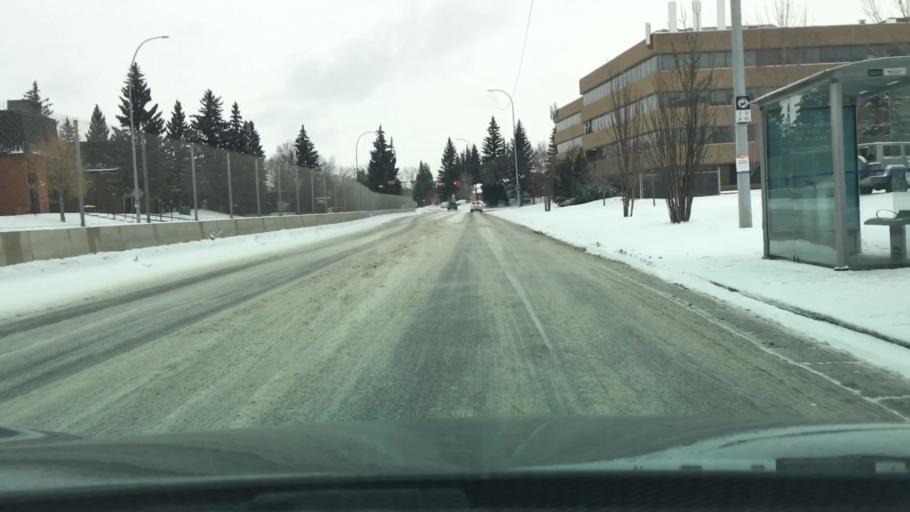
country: CA
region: Alberta
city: Calgary
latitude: 51.0867
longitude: -114.1587
